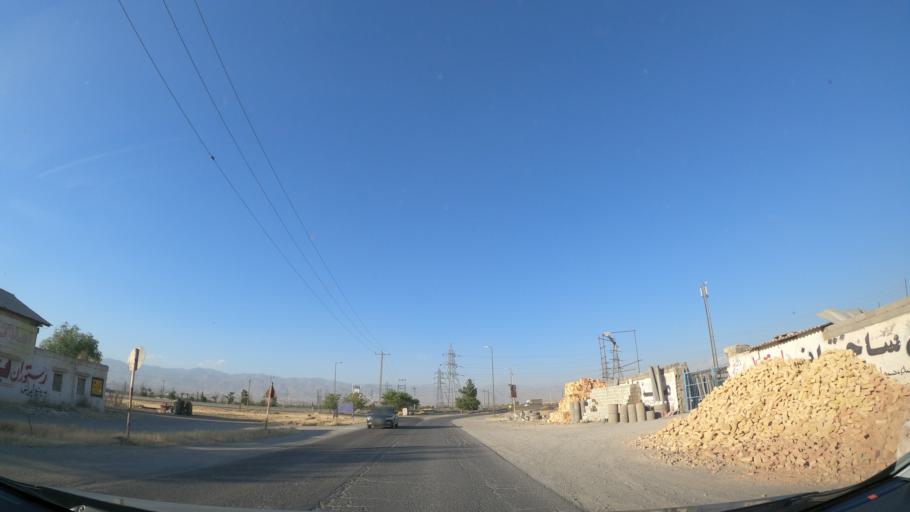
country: IR
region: Alborz
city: Hashtgerd
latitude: 35.9225
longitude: 50.7408
